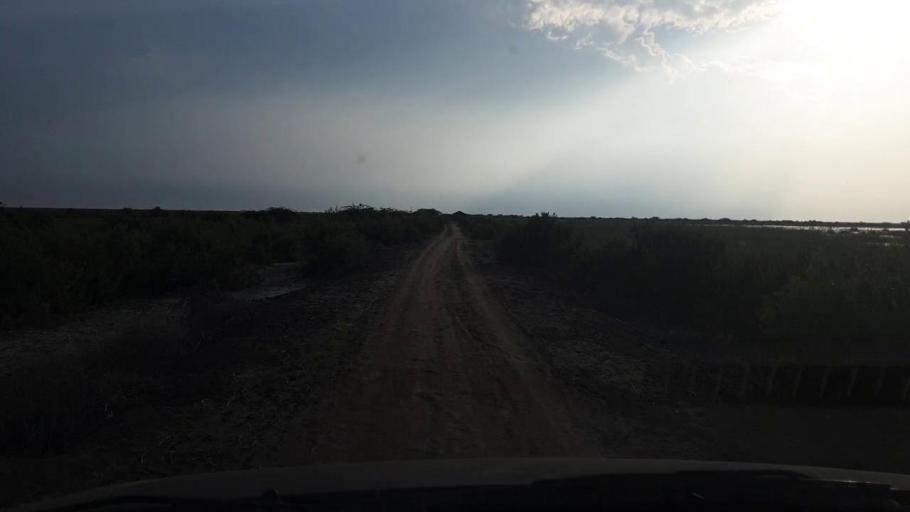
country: PK
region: Sindh
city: Badin
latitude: 24.4310
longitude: 68.6690
